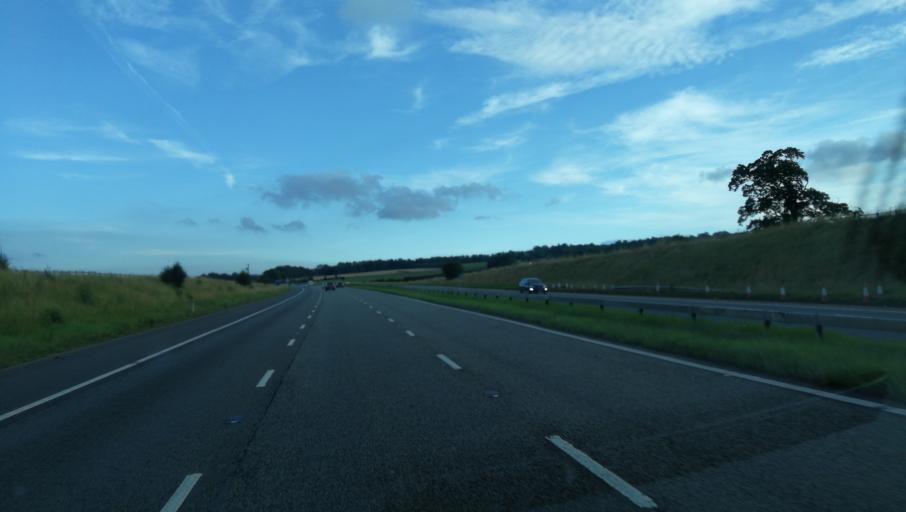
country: GB
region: England
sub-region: Cumbria
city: Penrith
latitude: 54.6226
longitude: -2.7215
